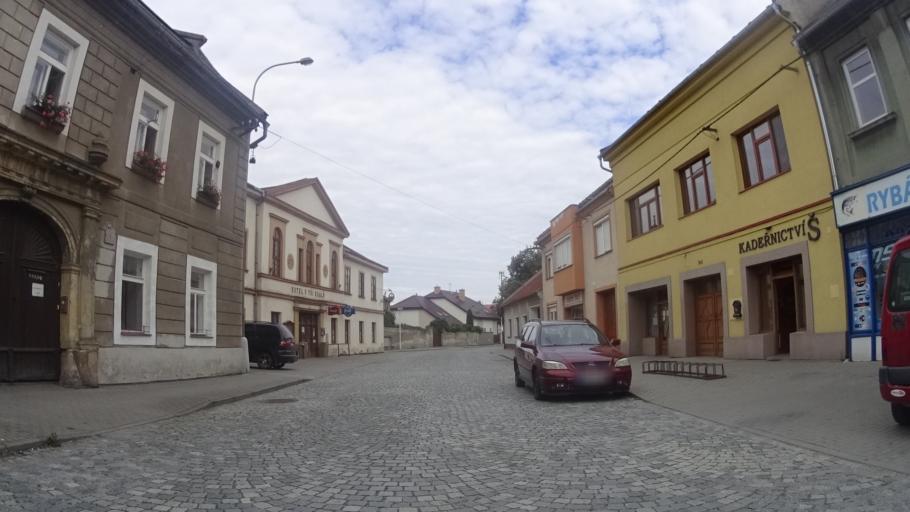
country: CZ
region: Olomoucky
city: Tovacov
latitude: 49.4298
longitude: 17.2893
